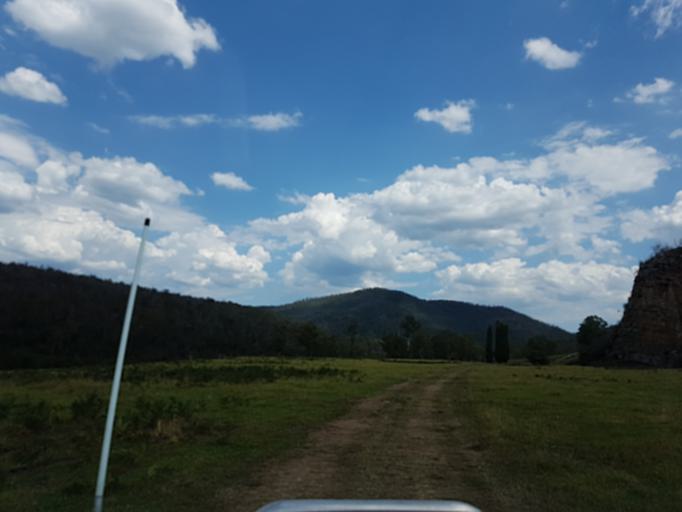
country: AU
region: Victoria
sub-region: East Gippsland
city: Lakes Entrance
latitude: -37.3988
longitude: 148.3347
